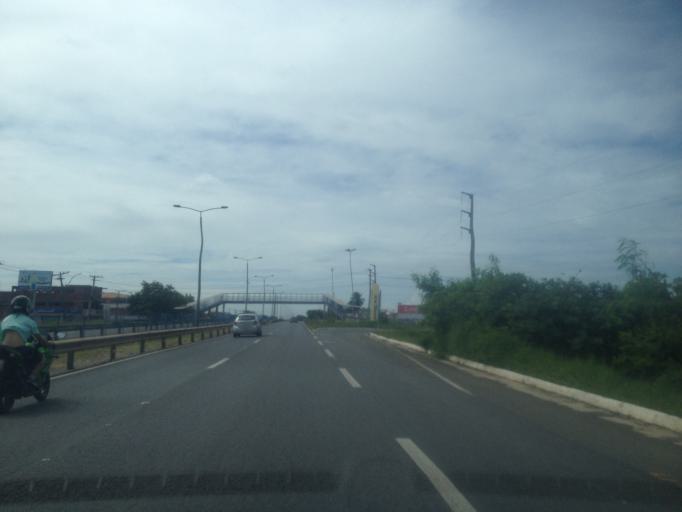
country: BR
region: Bahia
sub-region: Camacari
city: Camacari
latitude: -12.7677
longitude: -38.1882
